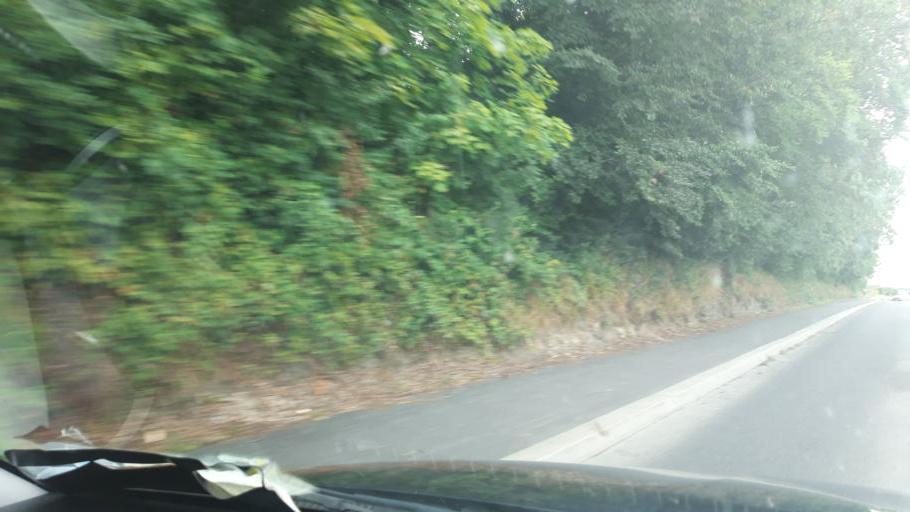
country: IE
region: Leinster
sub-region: Kilkenny
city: Kilkenny
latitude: 52.6374
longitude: -7.2711
